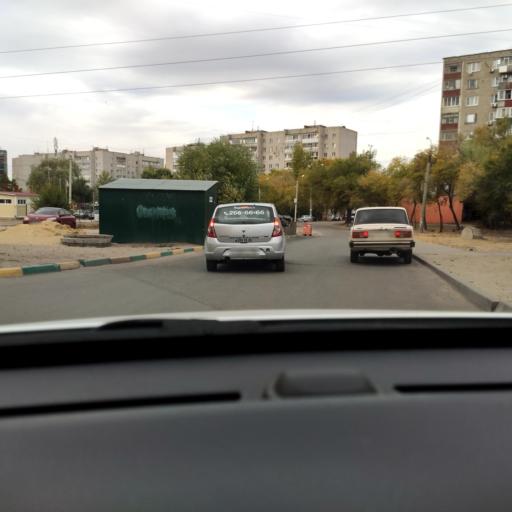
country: RU
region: Voronezj
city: Voronezh
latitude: 51.7184
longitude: 39.2656
